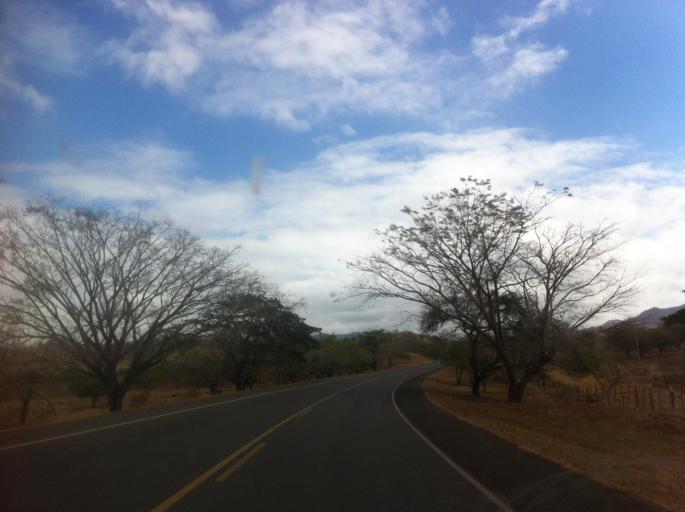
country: NI
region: Chontales
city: Acoyapa
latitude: 11.9905
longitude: -85.1686
